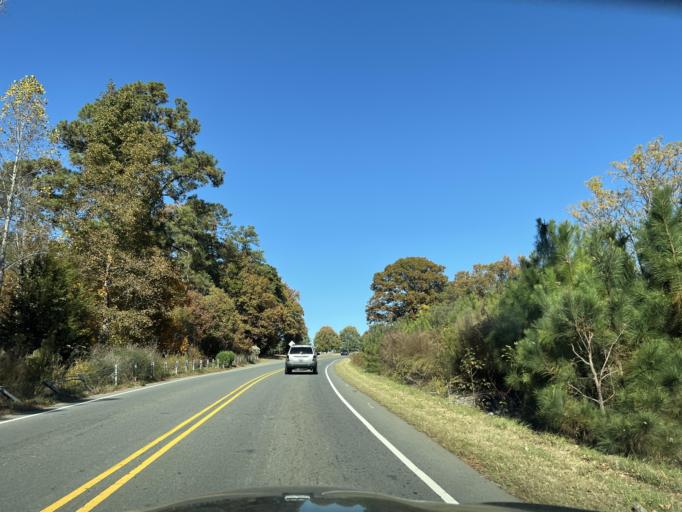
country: US
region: North Carolina
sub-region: Wake County
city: Raleigh
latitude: 35.7187
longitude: -78.6861
